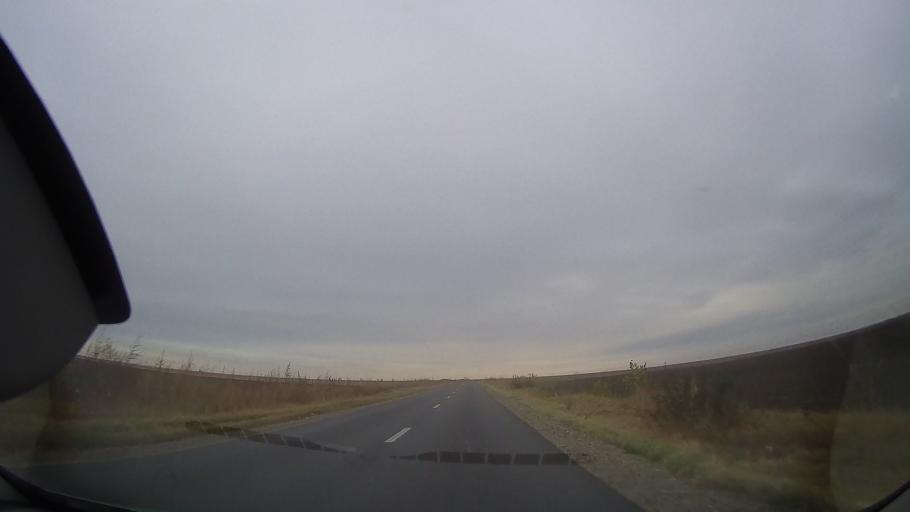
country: RO
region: Ialomita
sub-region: Oras Amara
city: Amara
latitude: 44.6434
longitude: 27.3006
